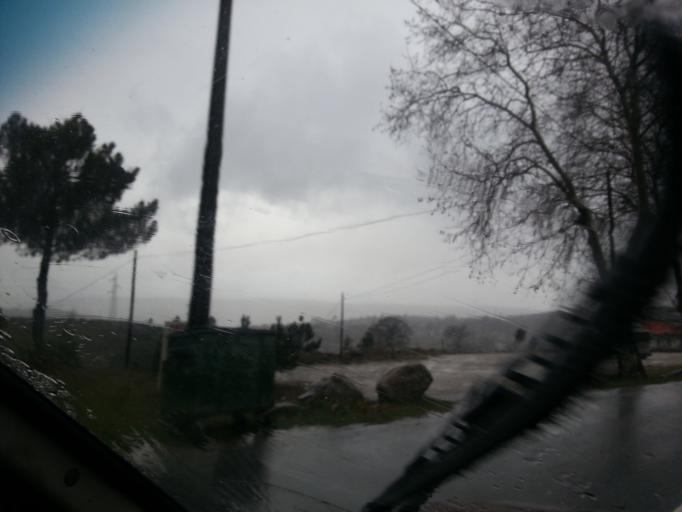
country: PT
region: Guarda
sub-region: Guarda
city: Guarda
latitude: 40.5394
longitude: -7.2941
